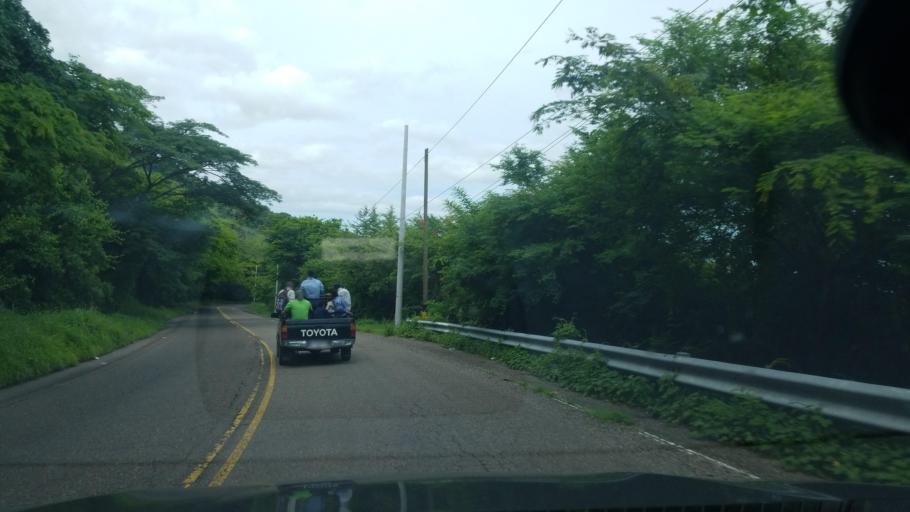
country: HN
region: Choluteca
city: Corpus
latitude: 13.3746
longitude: -87.0500
